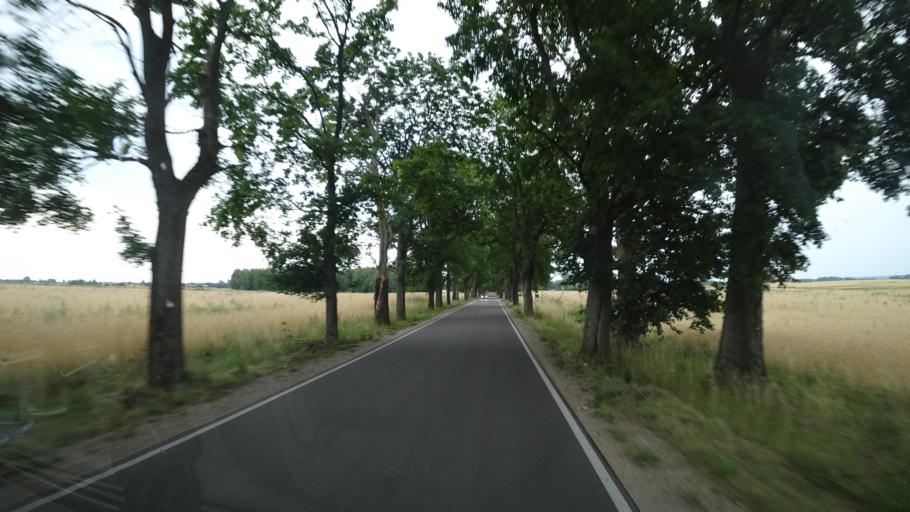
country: PL
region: Warmian-Masurian Voivodeship
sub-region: Powiat mragowski
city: Mikolajki
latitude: 53.8574
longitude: 21.6098
